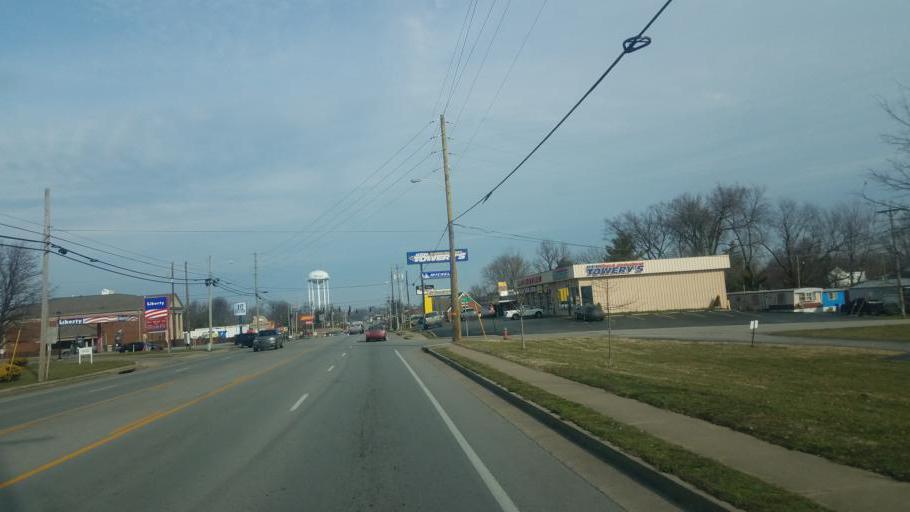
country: US
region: Kentucky
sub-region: Boyle County
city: Danville
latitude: 37.6269
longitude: -84.7747
